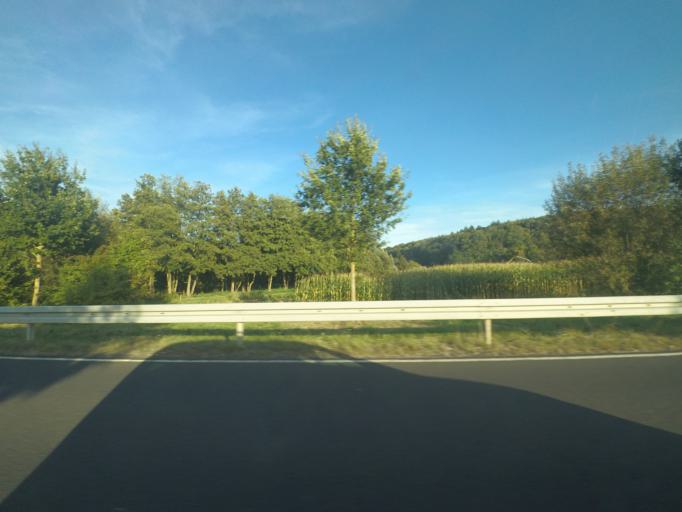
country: DE
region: Hesse
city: Hain-Grundau
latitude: 50.2373
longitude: 9.1474
